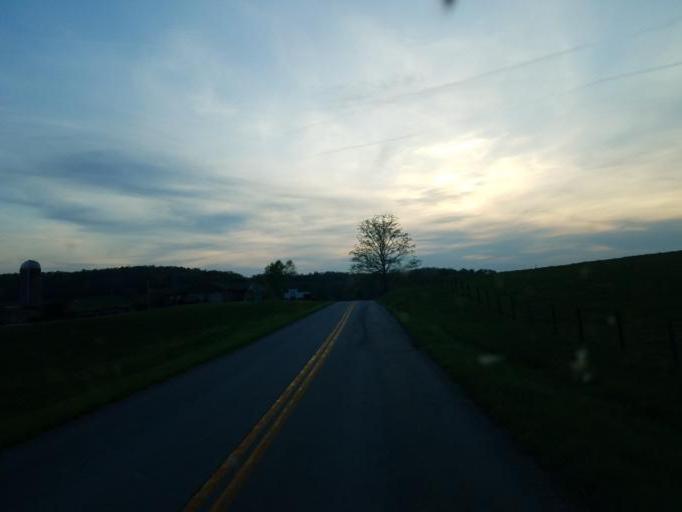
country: US
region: Kentucky
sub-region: Hart County
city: Munfordville
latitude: 37.2443
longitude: -85.7520
